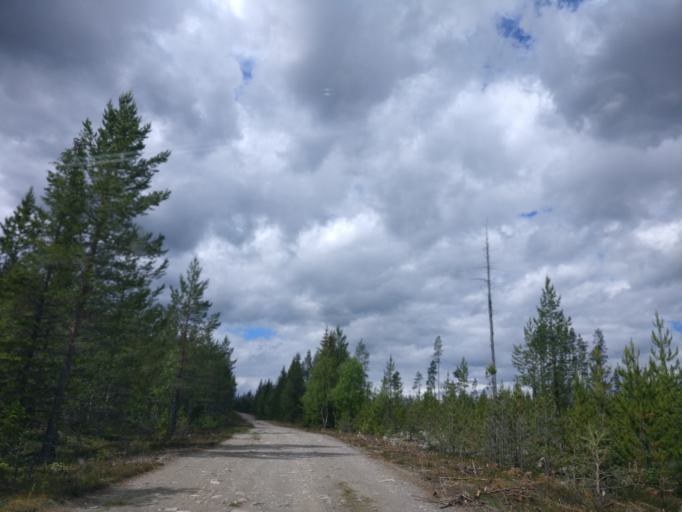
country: SE
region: Jaemtland
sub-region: Harjedalens Kommun
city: Sveg
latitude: 62.1963
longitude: 13.4132
